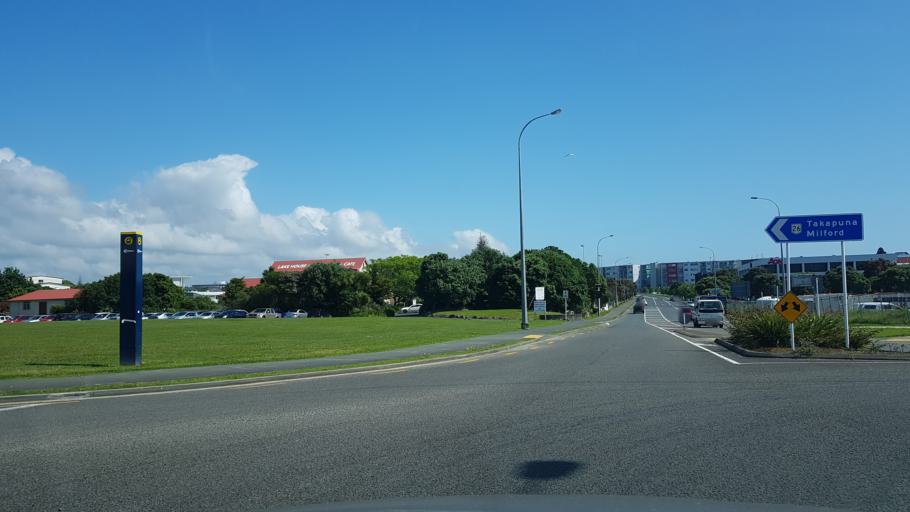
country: NZ
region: Auckland
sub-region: Auckland
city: North Shore
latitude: -36.7948
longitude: 174.7633
